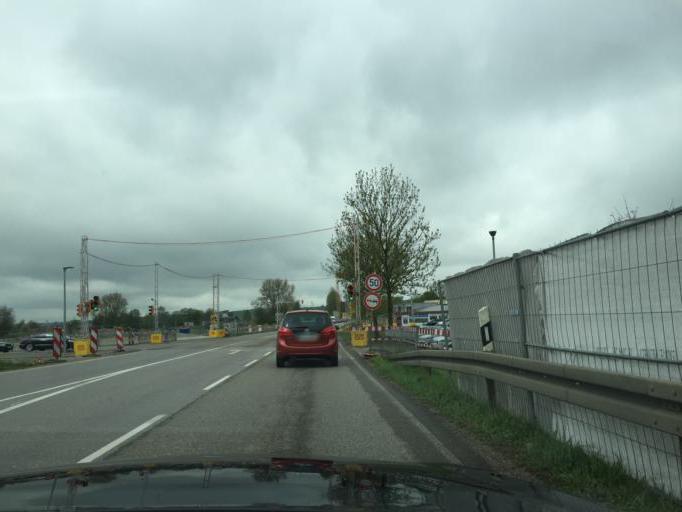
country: DE
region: Bavaria
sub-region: Swabia
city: Wertingen
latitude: 48.5532
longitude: 10.6872
